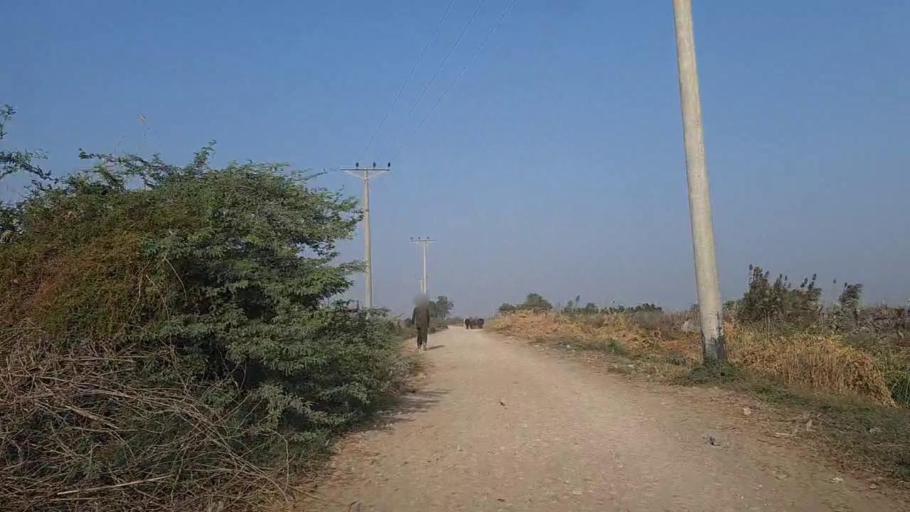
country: PK
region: Sindh
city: Keti Bandar
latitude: 24.1680
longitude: 67.6201
